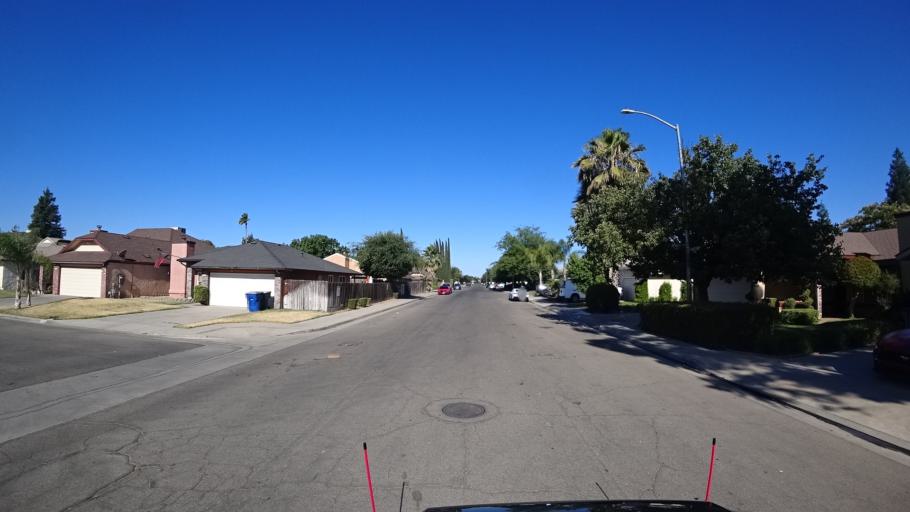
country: US
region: California
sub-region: Fresno County
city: West Park
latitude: 36.7752
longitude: -119.8587
